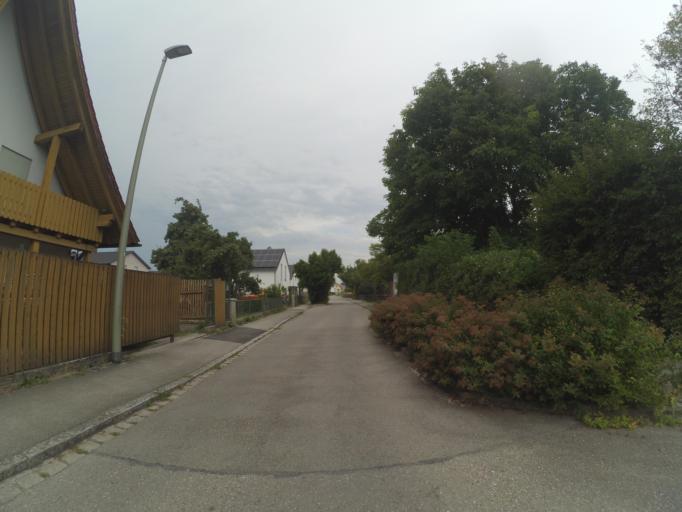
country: DE
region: Bavaria
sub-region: Swabia
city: Jengen
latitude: 48.0141
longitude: 10.7159
